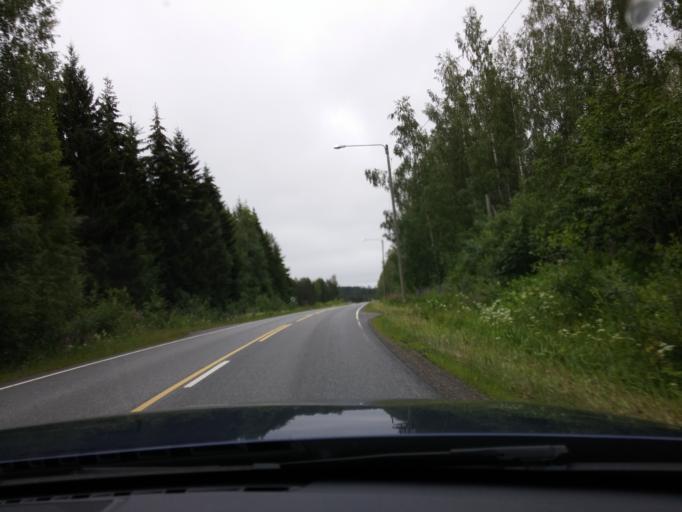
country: FI
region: Central Finland
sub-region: Joutsa
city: Joutsa
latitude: 61.8103
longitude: 25.9710
